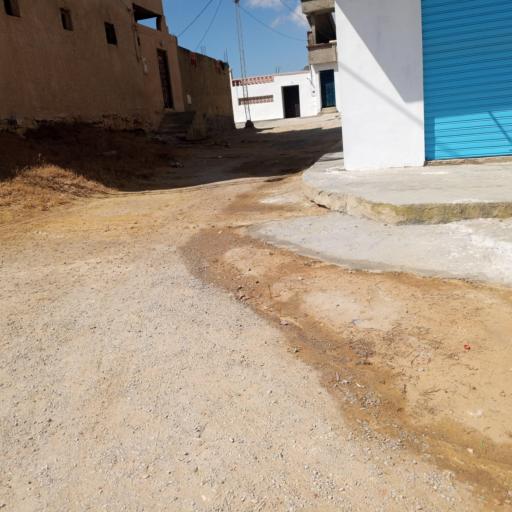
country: TN
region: Nabul
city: Qulaybiyah
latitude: 36.8573
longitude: 11.0336
